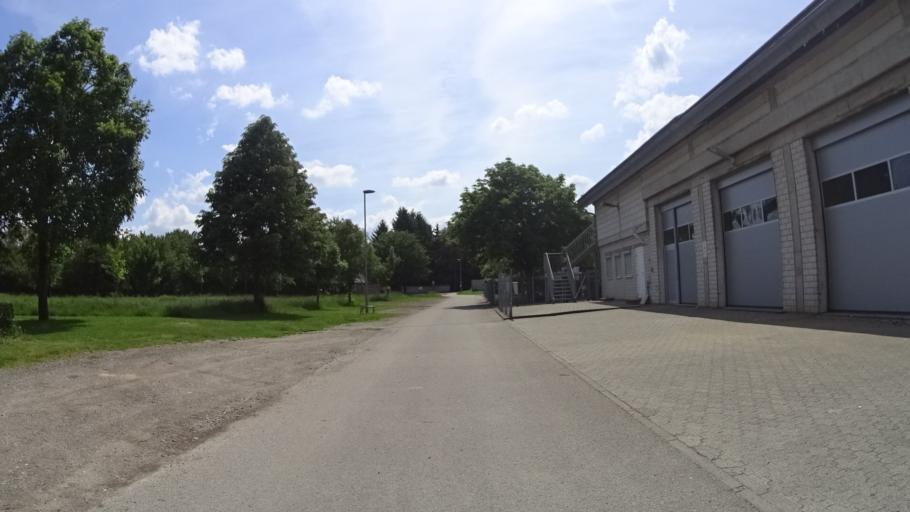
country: DE
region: Baden-Wuerttemberg
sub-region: Freiburg Region
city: Weisweil
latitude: 48.2061
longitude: 7.6811
